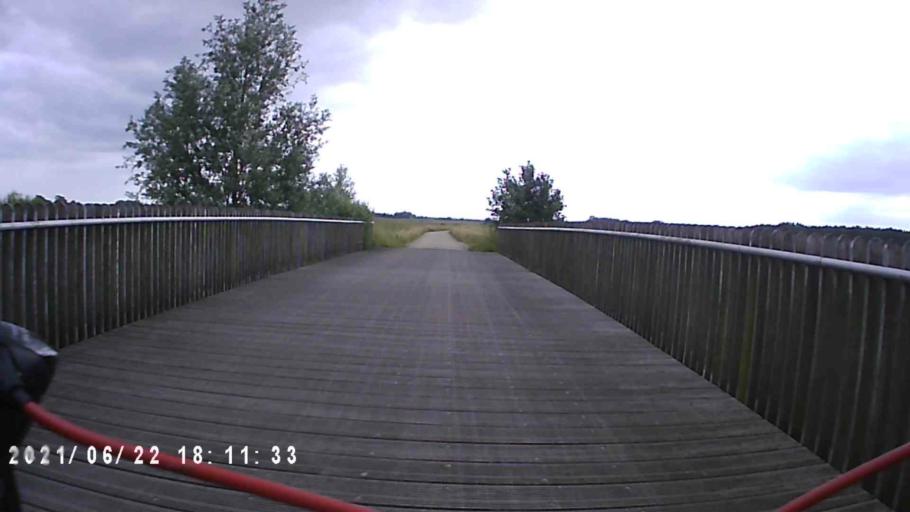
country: NL
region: Groningen
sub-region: Gemeente Groningen
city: Groningen
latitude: 53.1793
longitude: 6.4933
